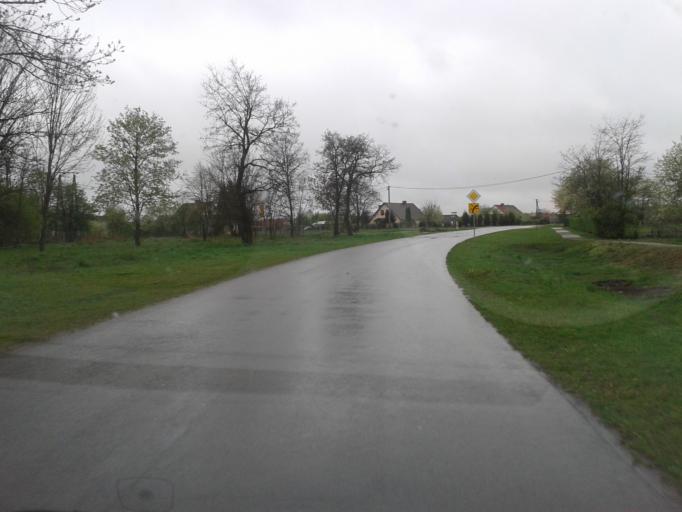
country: UA
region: Lviv
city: Uhniv
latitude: 50.3685
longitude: 23.6584
